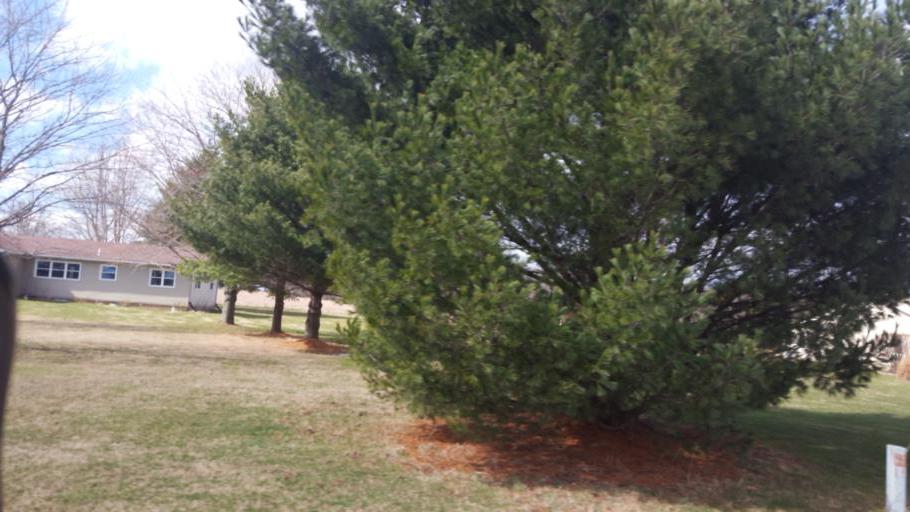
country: US
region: Ohio
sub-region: Knox County
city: Fredericktown
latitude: 40.5319
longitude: -82.5639
